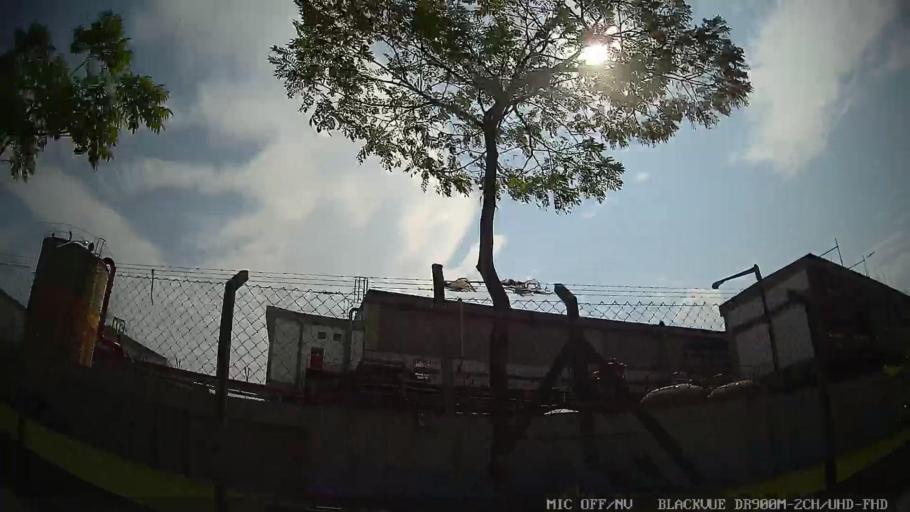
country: BR
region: Sao Paulo
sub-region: Itaquaquecetuba
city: Itaquaquecetuba
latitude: -23.4819
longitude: -46.4336
